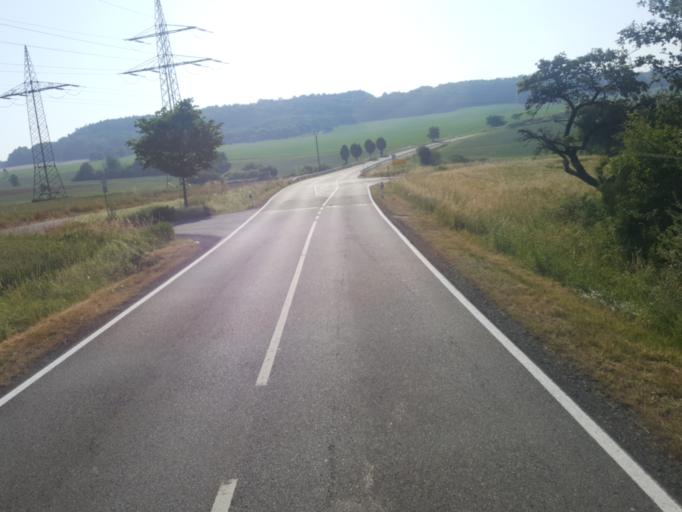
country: DE
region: Rheinland-Pfalz
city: Obererbach
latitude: 50.4549
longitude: 7.9576
